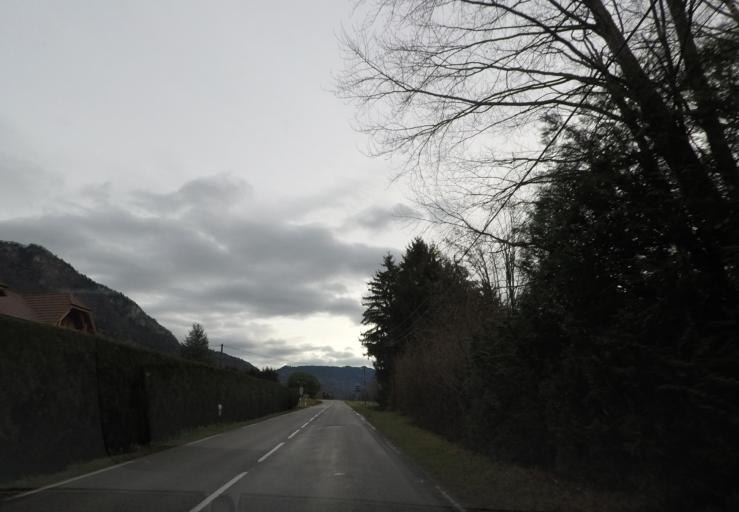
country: FR
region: Rhone-Alpes
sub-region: Departement de la Haute-Savoie
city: Thyez
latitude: 46.0893
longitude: 6.5316
